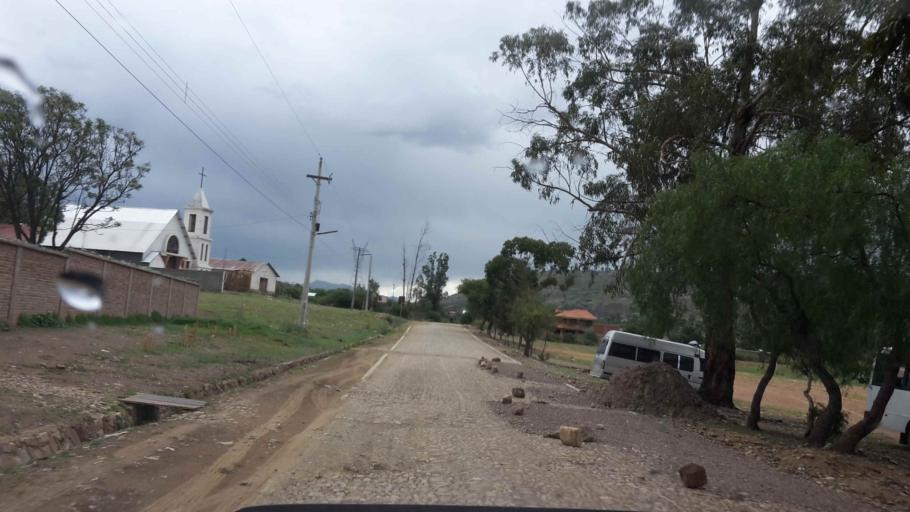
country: BO
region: Cochabamba
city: Cochabamba
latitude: -17.5451
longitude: -66.1887
